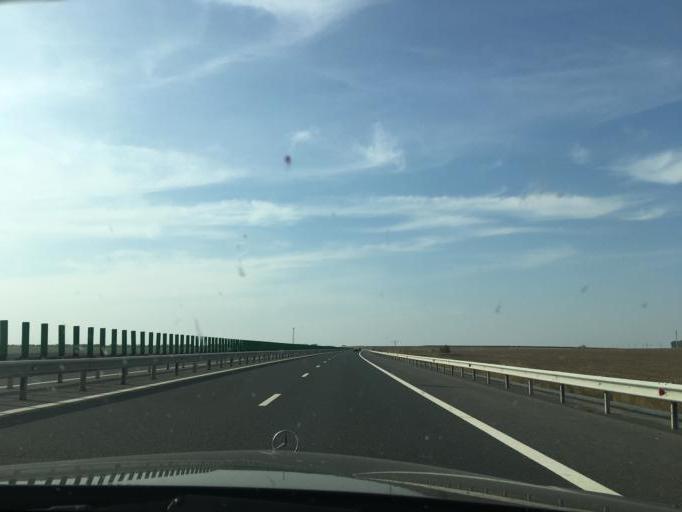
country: RO
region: Constanta
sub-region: Comuna Mircea Voda
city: Satu Nou
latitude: 44.2216
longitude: 28.1905
